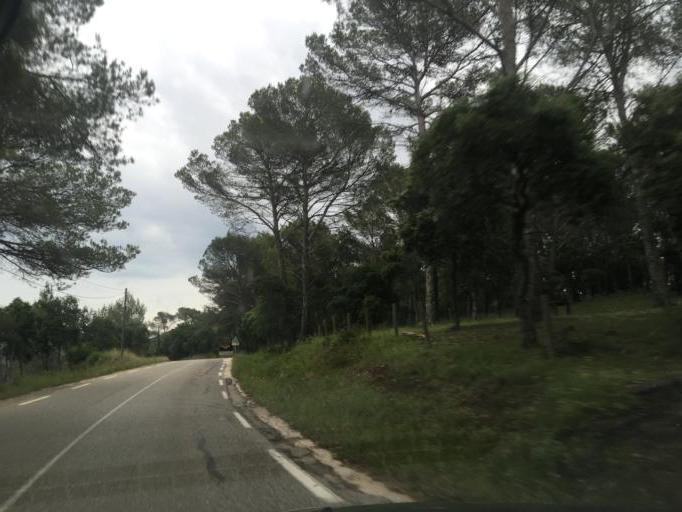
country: FR
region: Provence-Alpes-Cote d'Azur
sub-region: Departement du Var
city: Pierrefeu-du-Var
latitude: 43.2335
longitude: 6.2060
